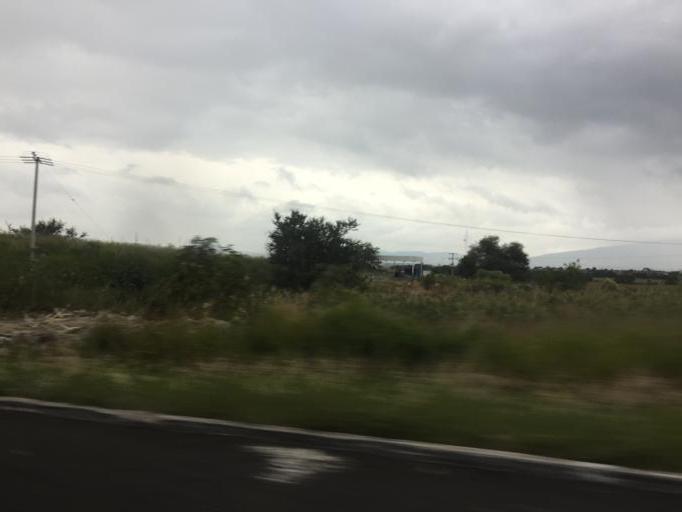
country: MX
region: Jalisco
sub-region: Zapotlan del Rey
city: Zapotlan del Rey
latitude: 20.4683
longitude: -102.9114
